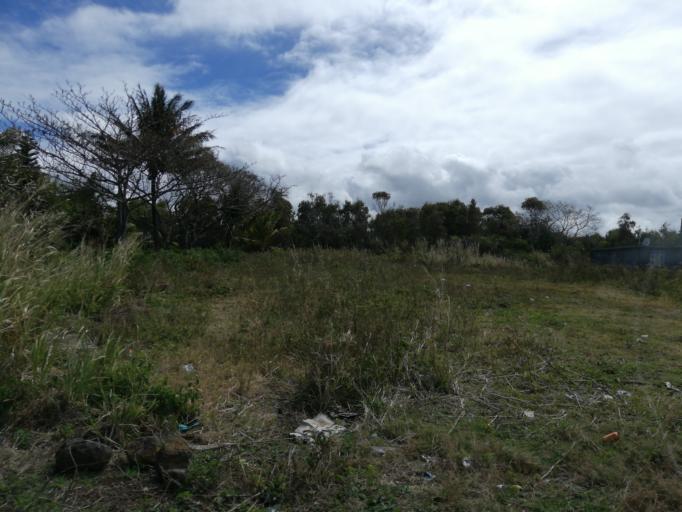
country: MU
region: Grand Port
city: Plaine Magnien
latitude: -20.4663
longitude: 57.6790
